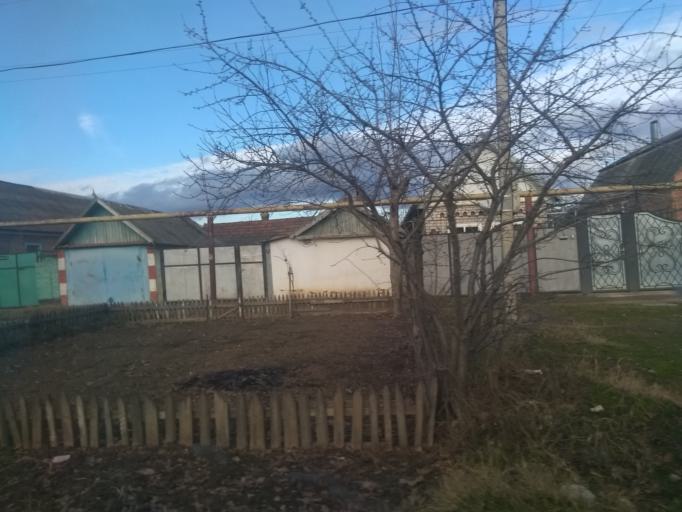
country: RU
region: Stavropol'skiy
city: Krasnokumskoye
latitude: 44.1765
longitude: 43.4811
